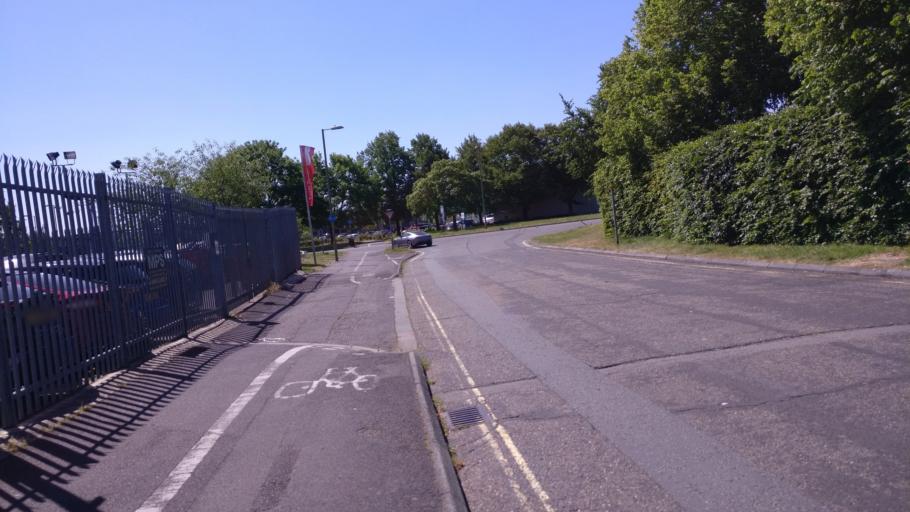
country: GB
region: England
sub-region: Hampshire
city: Basingstoke
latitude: 51.2750
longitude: -1.1059
